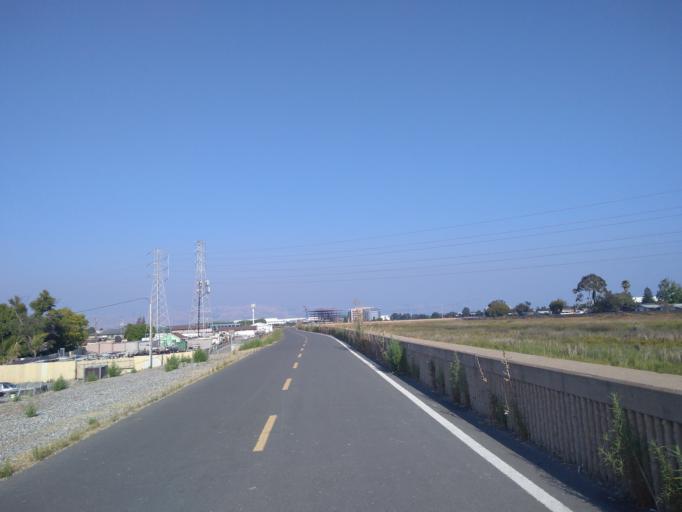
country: US
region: California
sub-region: Santa Clara County
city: Milpitas
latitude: 37.4233
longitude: -121.9755
